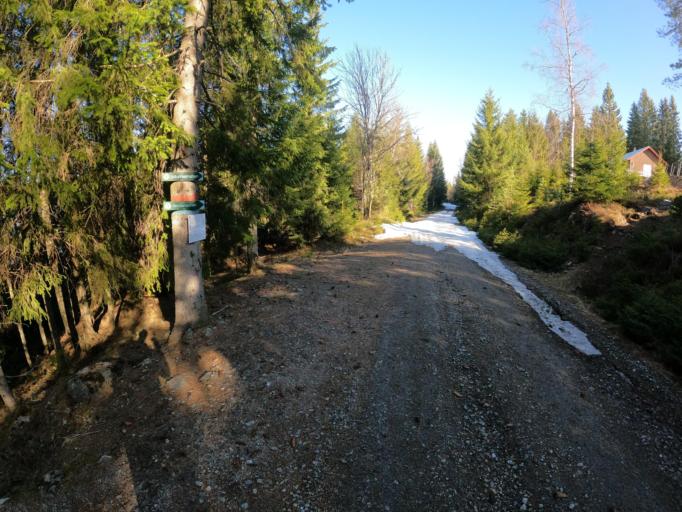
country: NO
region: Akershus
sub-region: Nittedal
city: Aneby
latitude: 60.1582
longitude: 10.8964
